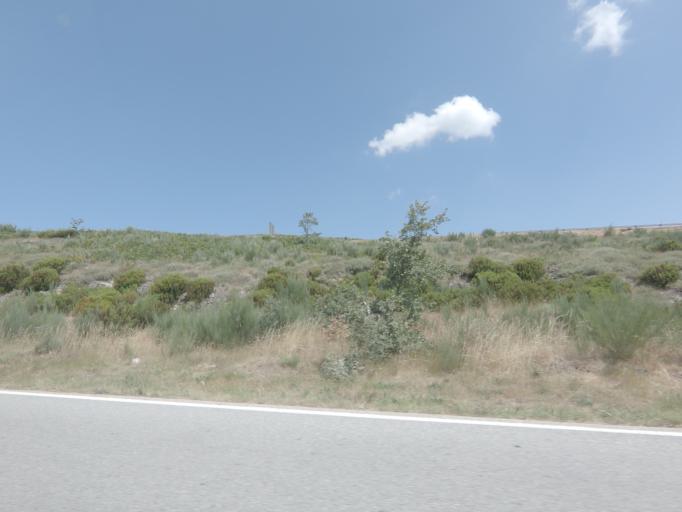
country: PT
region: Viseu
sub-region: Castro Daire
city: Castro Daire
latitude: 40.9903
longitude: -7.8839
